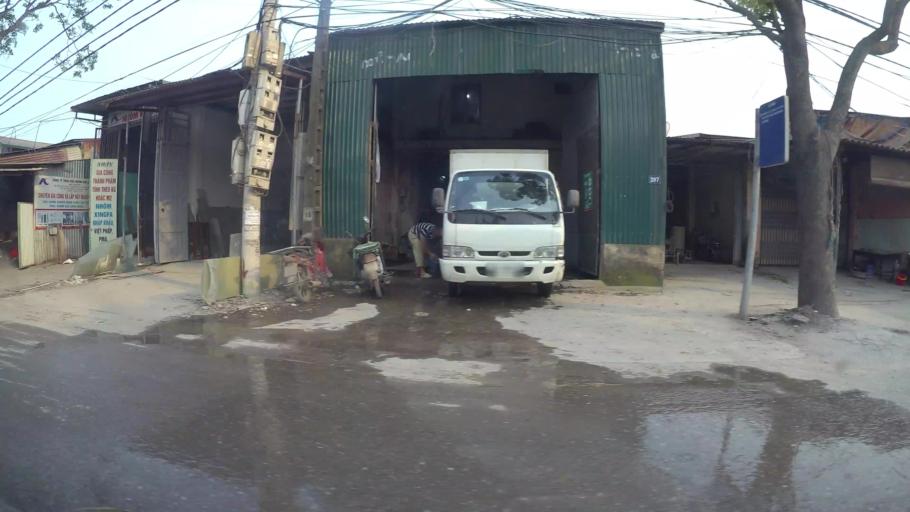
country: VN
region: Ha Noi
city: Ha Dong
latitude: 20.9952
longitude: 105.7427
